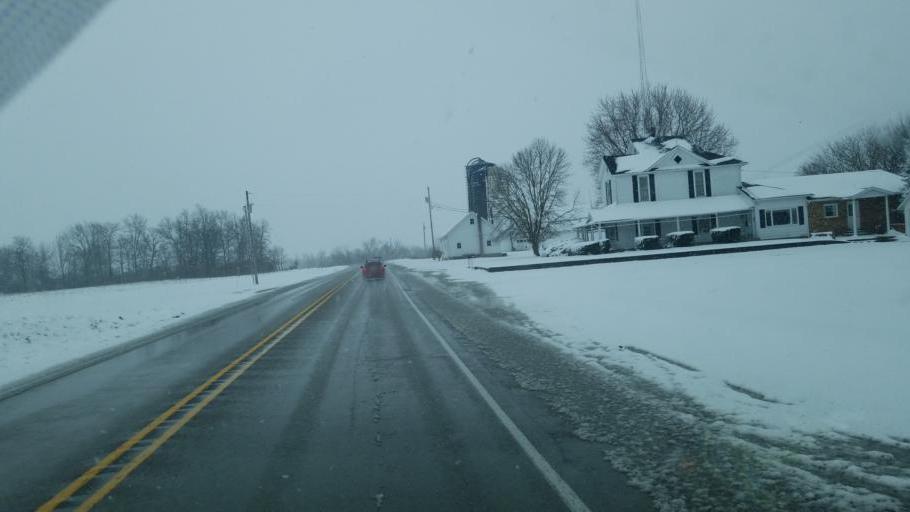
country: US
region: Indiana
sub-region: Randolph County
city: Parker City
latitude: 40.0803
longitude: -85.2748
